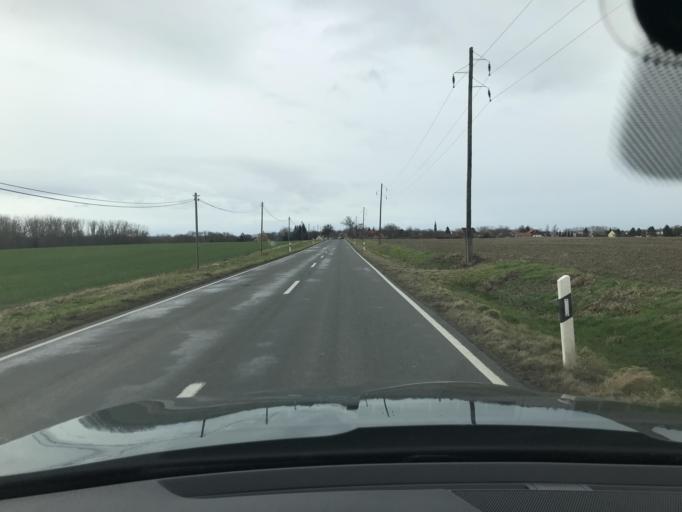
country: DE
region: Saxony-Anhalt
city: Wegeleben
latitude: 51.8881
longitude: 11.1950
